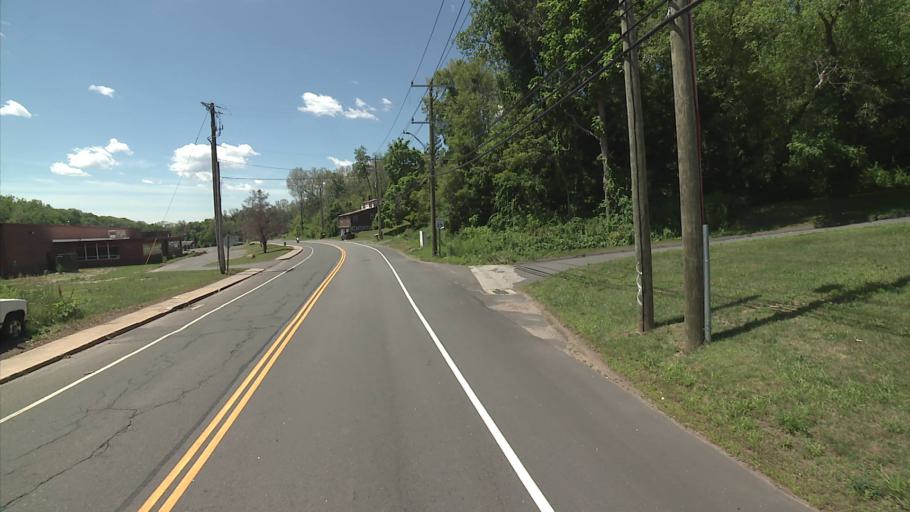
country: US
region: Connecticut
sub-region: Middlesex County
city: East Hampton
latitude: 41.5734
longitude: -72.5025
